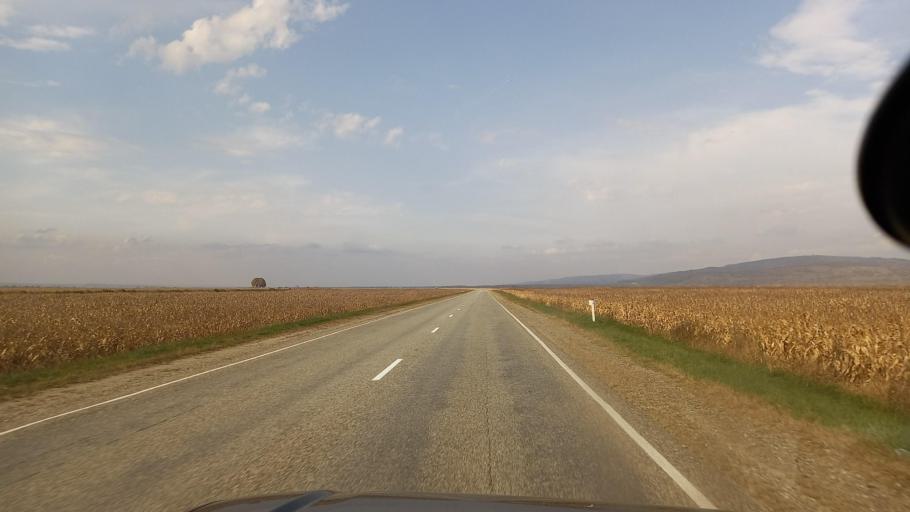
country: RU
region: Krasnodarskiy
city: Shedok
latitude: 44.2884
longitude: 40.8658
